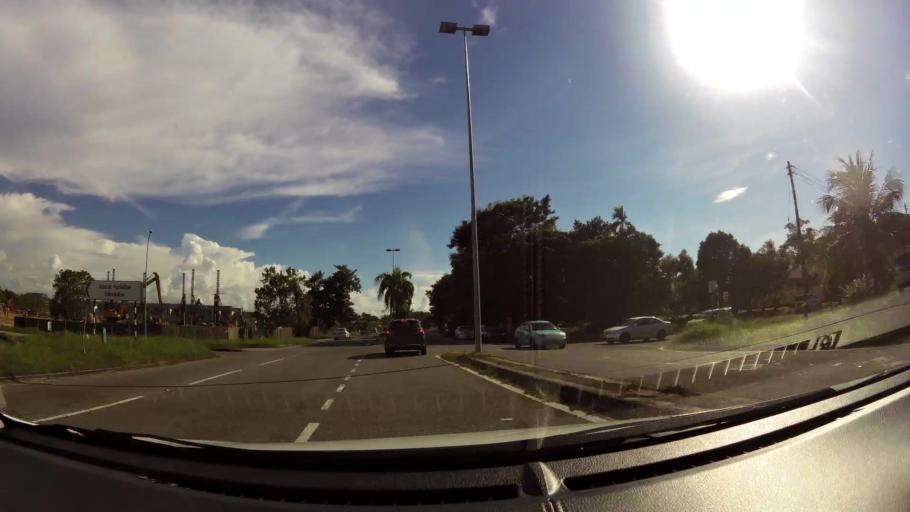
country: BN
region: Brunei and Muara
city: Bandar Seri Begawan
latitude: 4.9660
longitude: 114.9622
